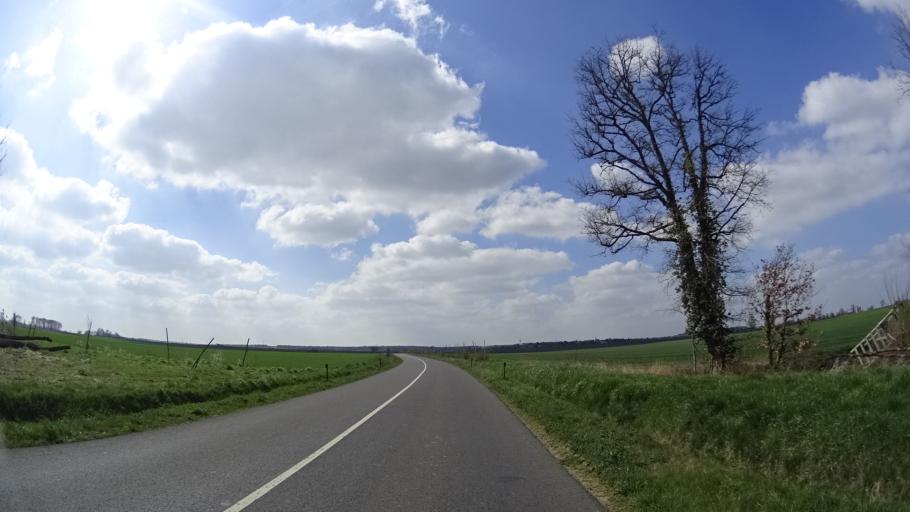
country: FR
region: Pays de la Loire
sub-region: Departement de Maine-et-Loire
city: Breze
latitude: 47.0860
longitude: -0.0104
